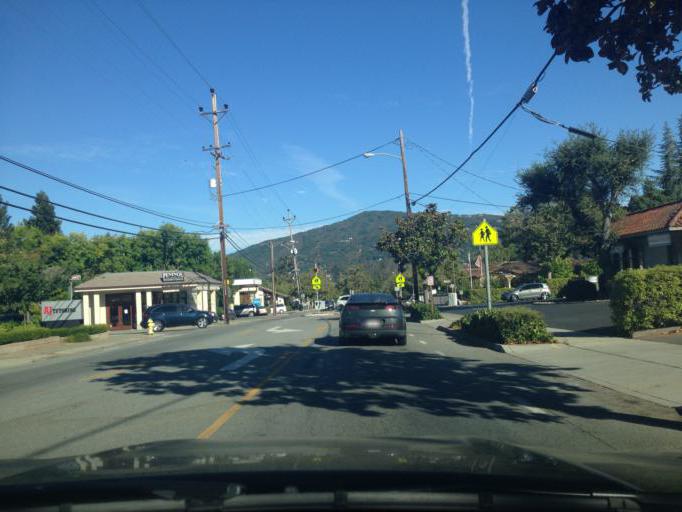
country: US
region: California
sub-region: Santa Clara County
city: Monte Sereno
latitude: 37.2309
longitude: -121.9840
